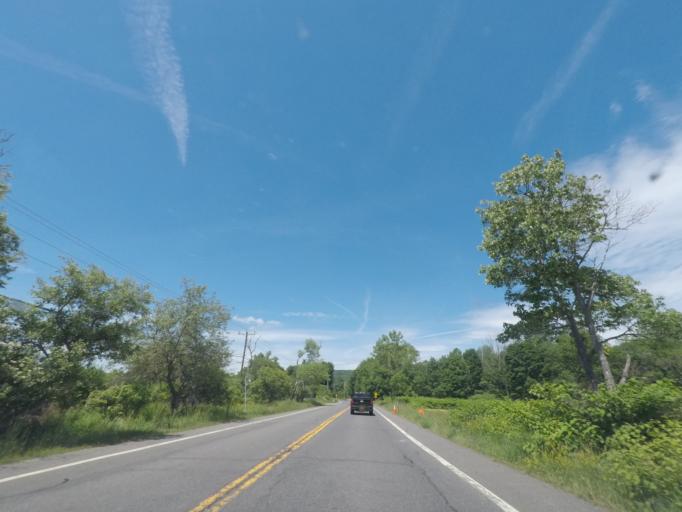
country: US
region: Massachusetts
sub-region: Berkshire County
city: Housatonic
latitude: 42.2248
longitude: -73.5056
